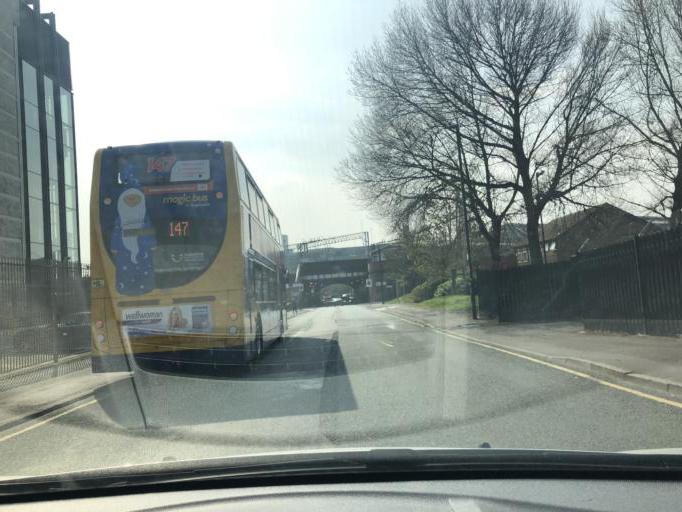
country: GB
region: England
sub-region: Manchester
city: Manchester
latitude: 53.4774
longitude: -2.2242
